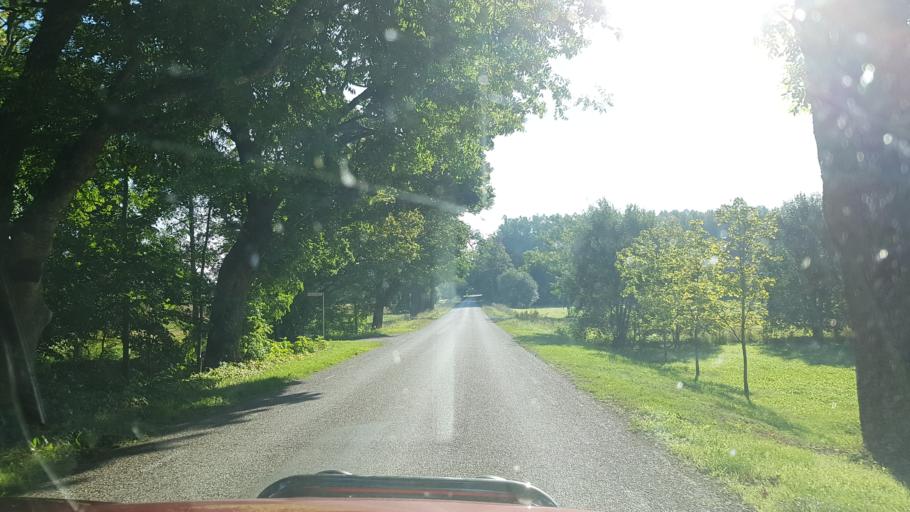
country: EE
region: Jogevamaa
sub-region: Tabivere vald
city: Tabivere
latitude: 58.6692
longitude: 26.7676
